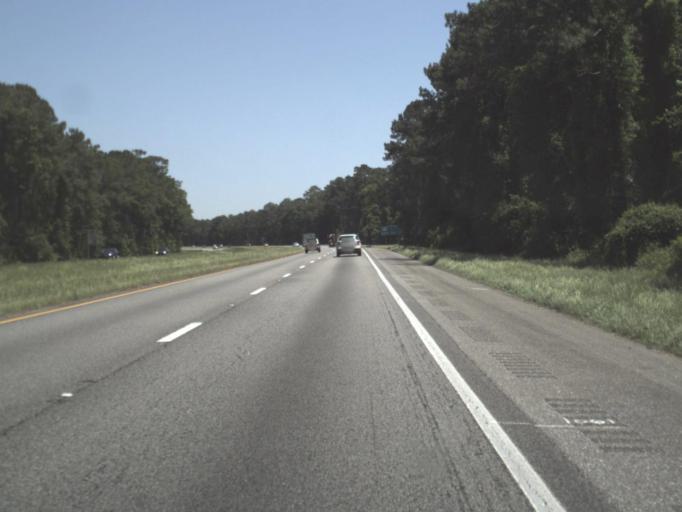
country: US
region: Florida
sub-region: Jefferson County
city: Monticello
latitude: 30.4477
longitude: -83.7461
